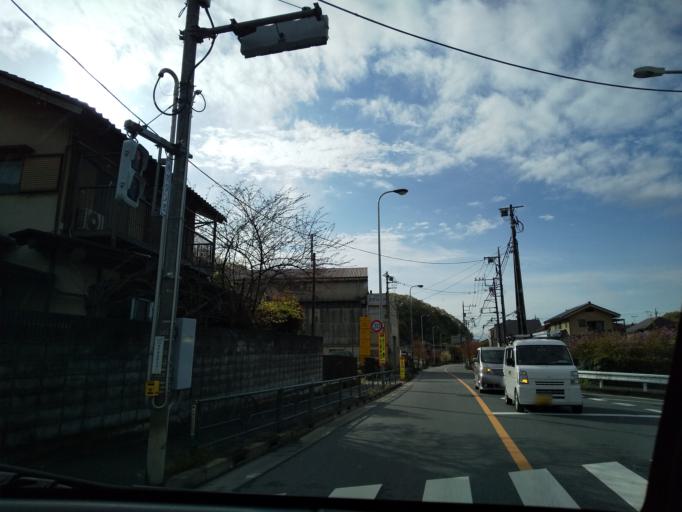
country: JP
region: Tokyo
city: Itsukaichi
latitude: 35.6892
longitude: 139.2505
